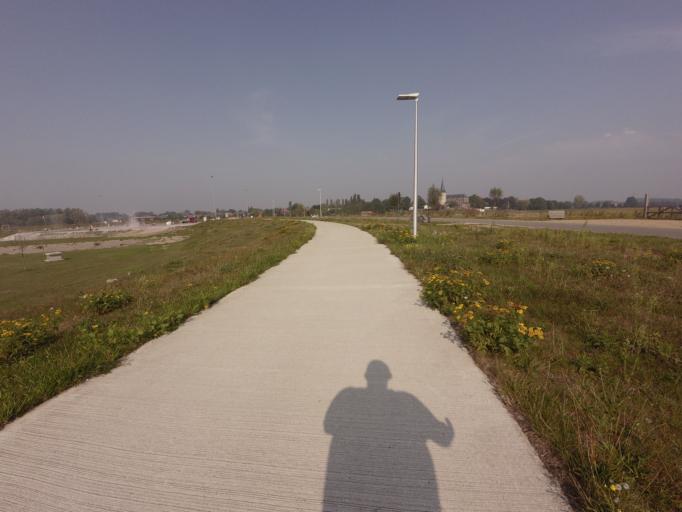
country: NL
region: Limburg
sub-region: Gemeente Maasgouw
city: Maasbracht
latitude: 51.1470
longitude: 5.8266
